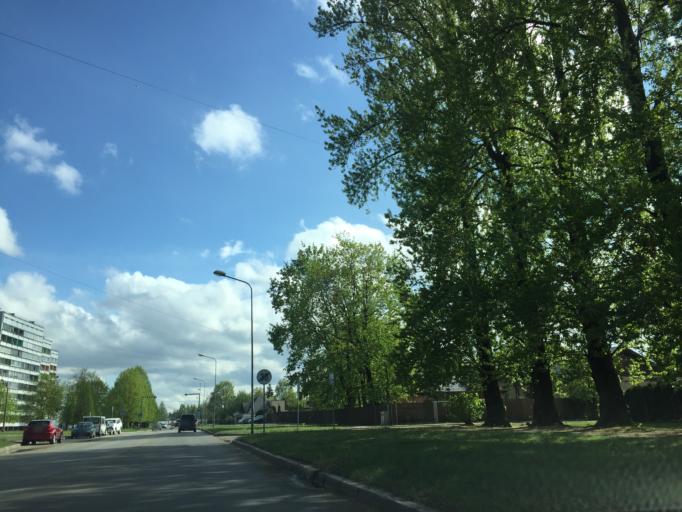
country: LV
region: Riga
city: Riga
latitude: 56.9358
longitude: 24.1951
